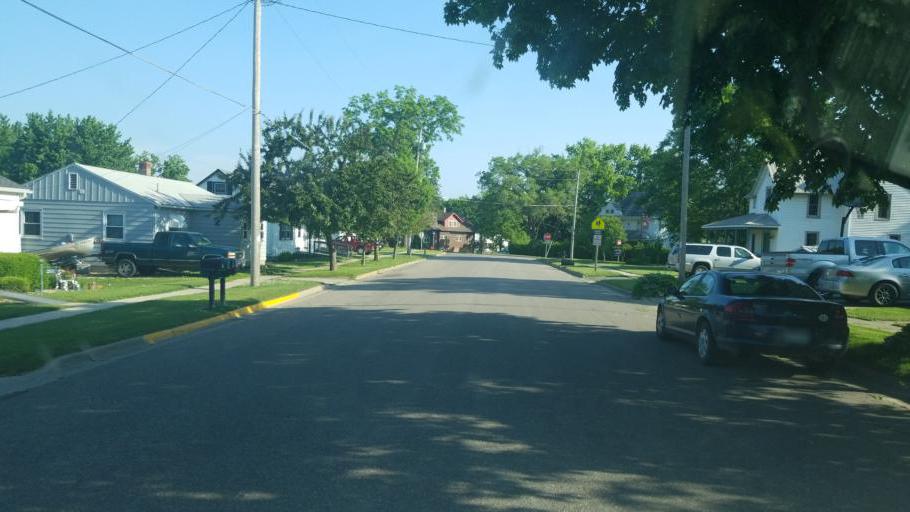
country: US
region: Wisconsin
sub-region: Vernon County
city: Hillsboro
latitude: 43.6554
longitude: -90.3456
